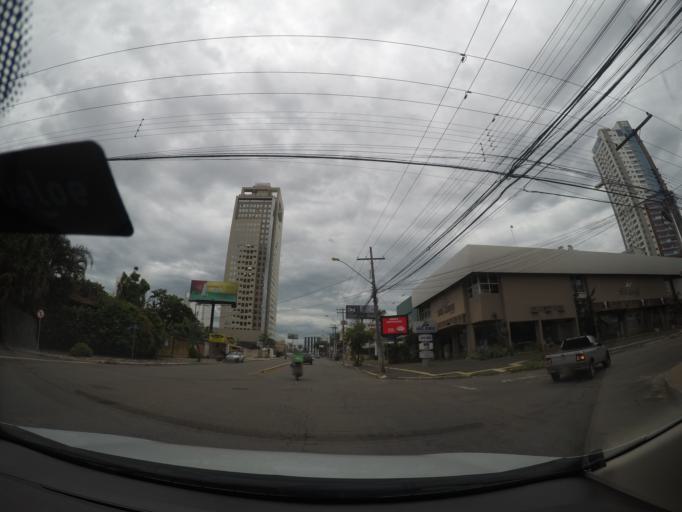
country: BR
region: Goias
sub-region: Goiania
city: Goiania
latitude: -16.7046
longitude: -49.2669
